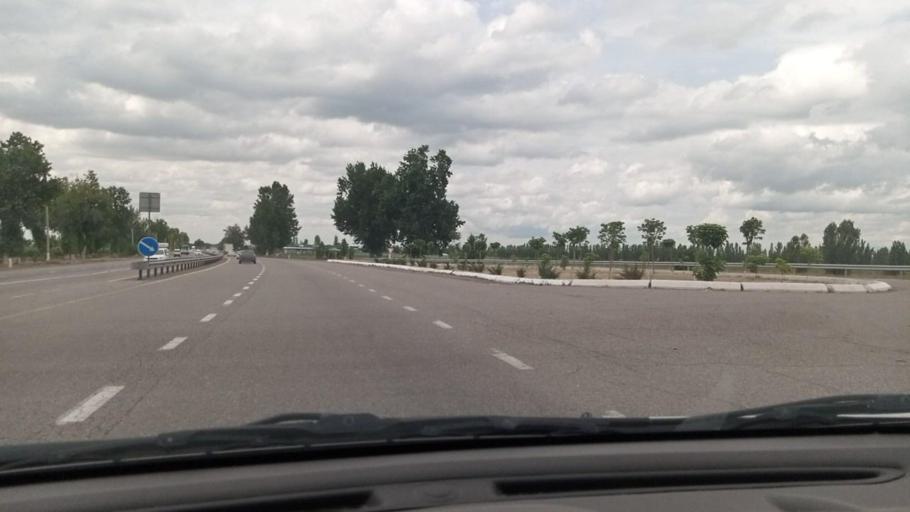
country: UZ
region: Toshkent Shahri
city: Bektemir
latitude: 41.1436
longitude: 69.4322
